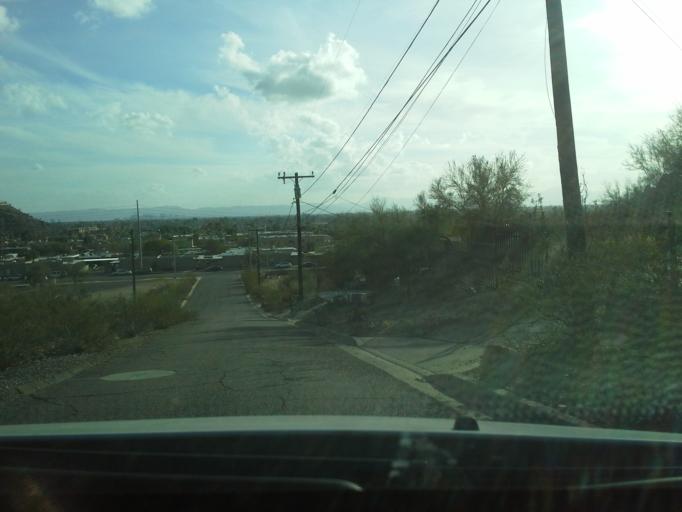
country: US
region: Arizona
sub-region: Maricopa County
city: Glendale
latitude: 33.5838
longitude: -112.0861
